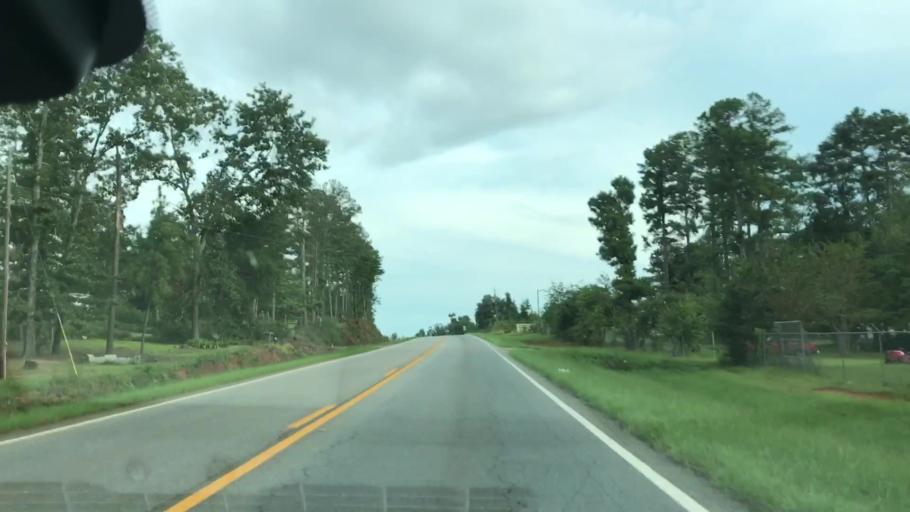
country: US
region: Georgia
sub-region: Quitman County
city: Georgetown
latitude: 31.8634
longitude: -85.0715
